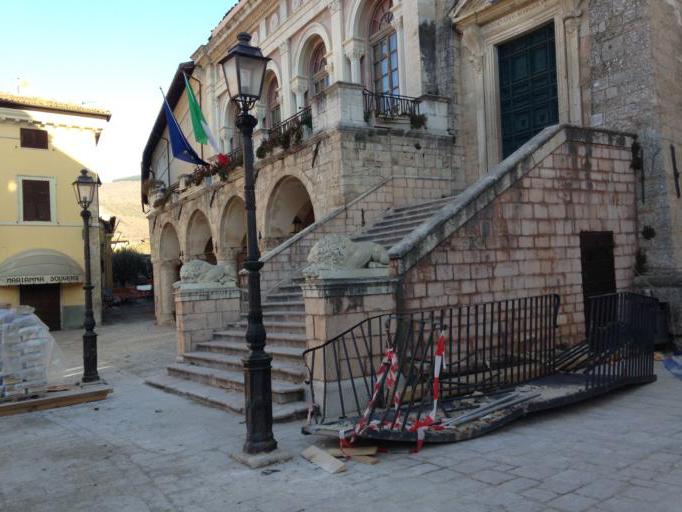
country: IT
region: Umbria
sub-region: Provincia di Perugia
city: Norcia
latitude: 42.7923
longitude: 13.0931
